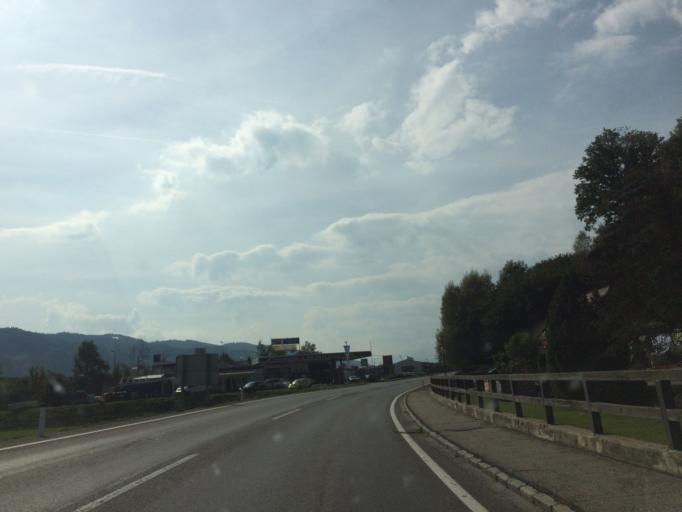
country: AT
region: Styria
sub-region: Politischer Bezirk Murtal
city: Feistritz bei Knittelfeld
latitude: 47.2604
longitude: 14.9019
